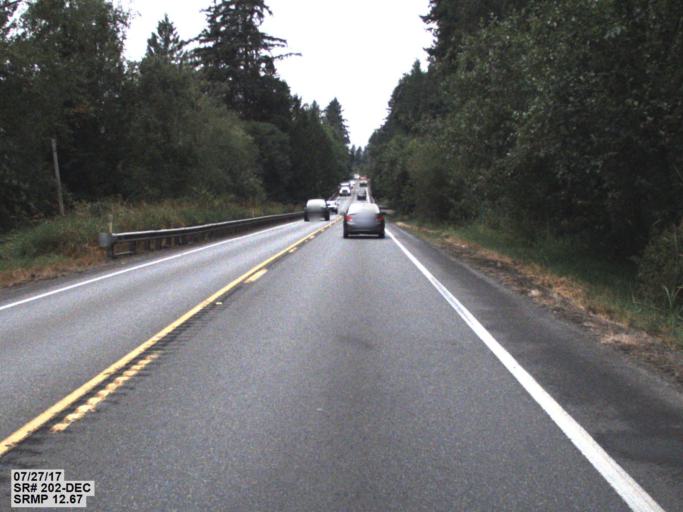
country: US
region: Washington
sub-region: King County
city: Union Hill-Novelty Hill
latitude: 47.6422
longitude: -122.0165
